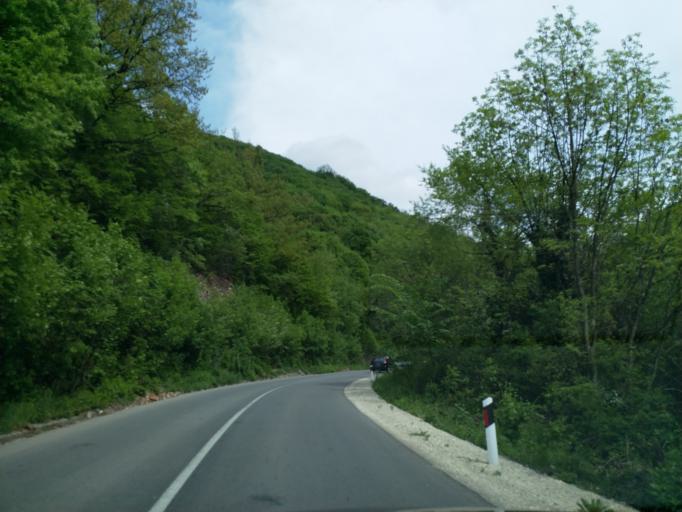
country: RS
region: Central Serbia
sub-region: Pomoravski Okrug
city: Despotovac
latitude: 43.9756
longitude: 21.5095
